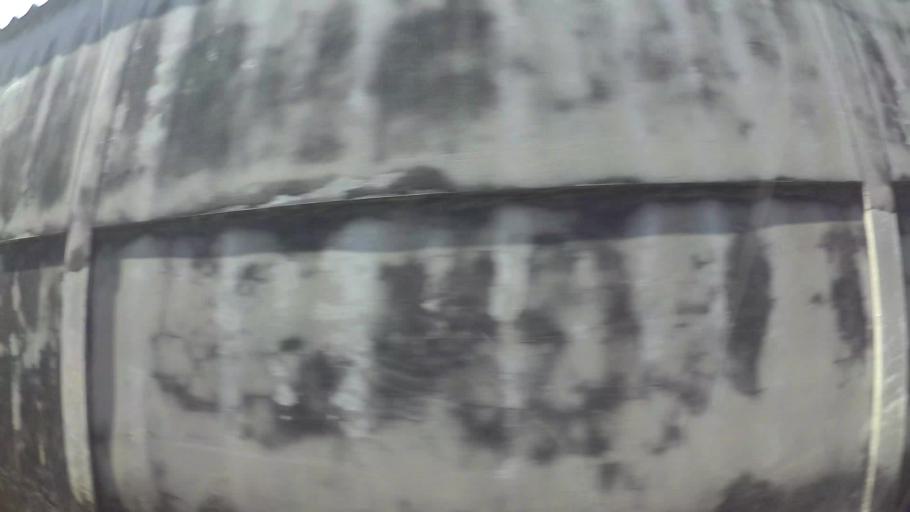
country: TH
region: Rayong
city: Rayong
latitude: 12.6712
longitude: 101.3001
